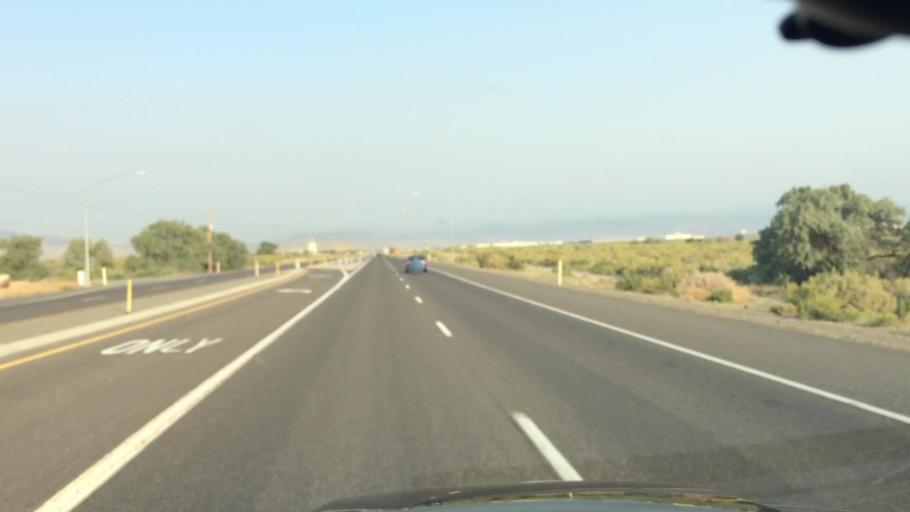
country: US
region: Nevada
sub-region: Lyon County
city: Fernley
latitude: 39.5943
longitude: -119.1664
